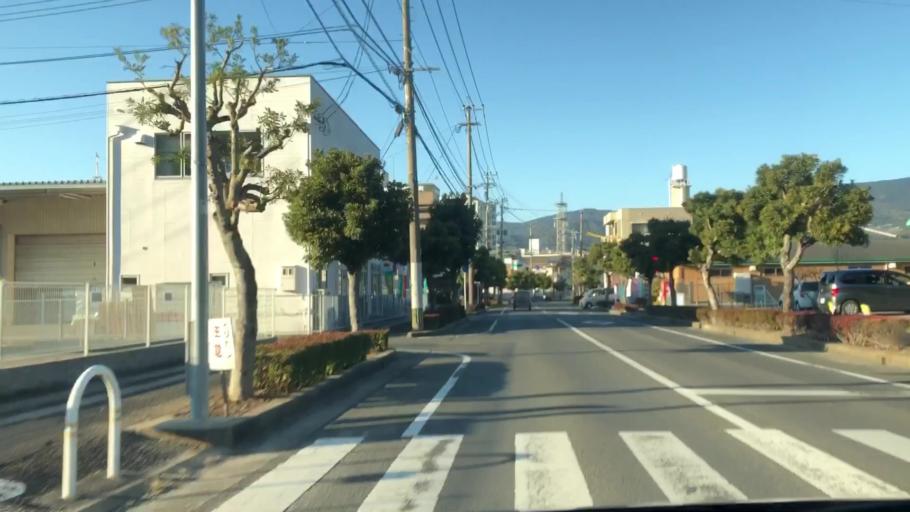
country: JP
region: Nagasaki
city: Sasebo
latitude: 33.1284
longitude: 129.8006
